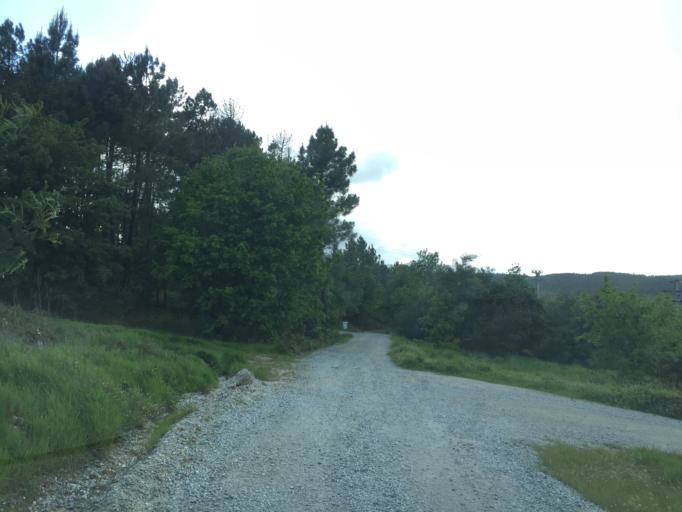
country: PT
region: Viseu
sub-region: Viseu
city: Abraveses
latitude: 40.6680
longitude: -7.9386
